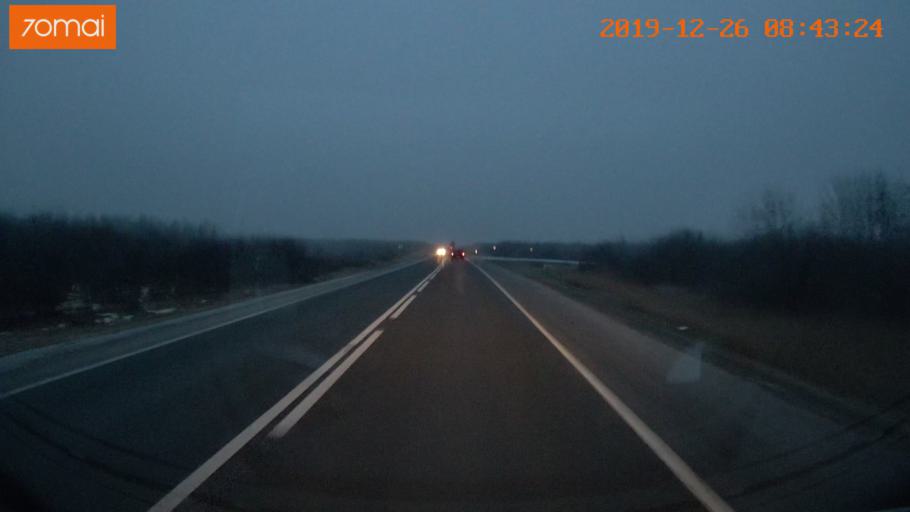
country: RU
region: Jaroslavl
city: Prechistoye
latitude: 58.5724
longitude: 40.3537
